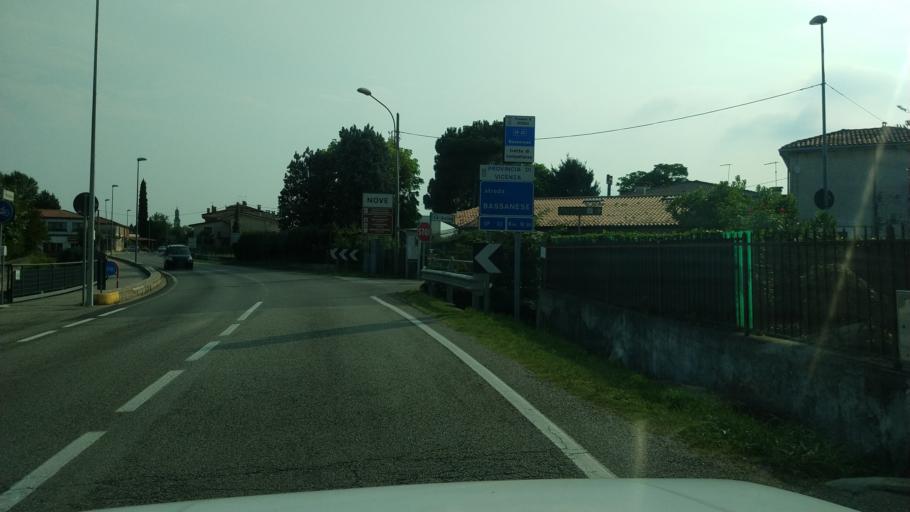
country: IT
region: Veneto
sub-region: Provincia di Vicenza
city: Nove
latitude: 45.7349
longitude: 11.6877
